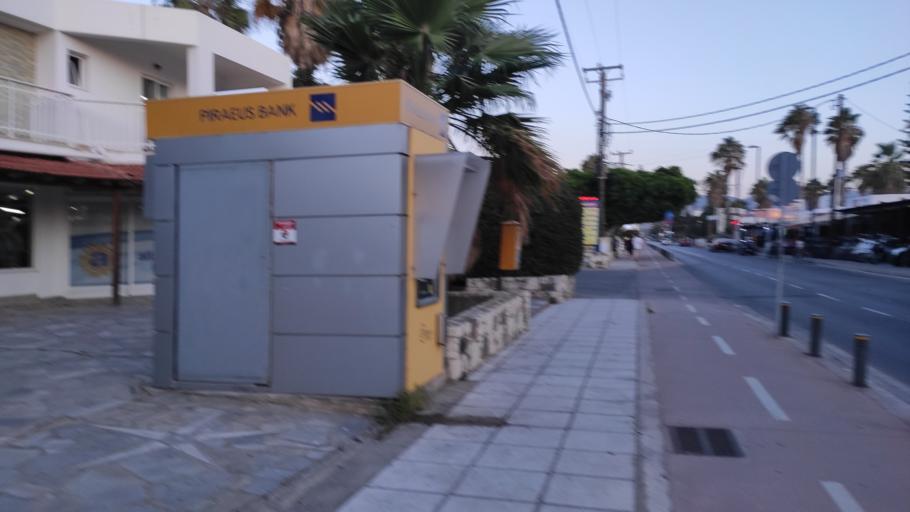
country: GR
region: South Aegean
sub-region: Nomos Dodekanisou
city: Kos
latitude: 36.9125
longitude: 27.2785
